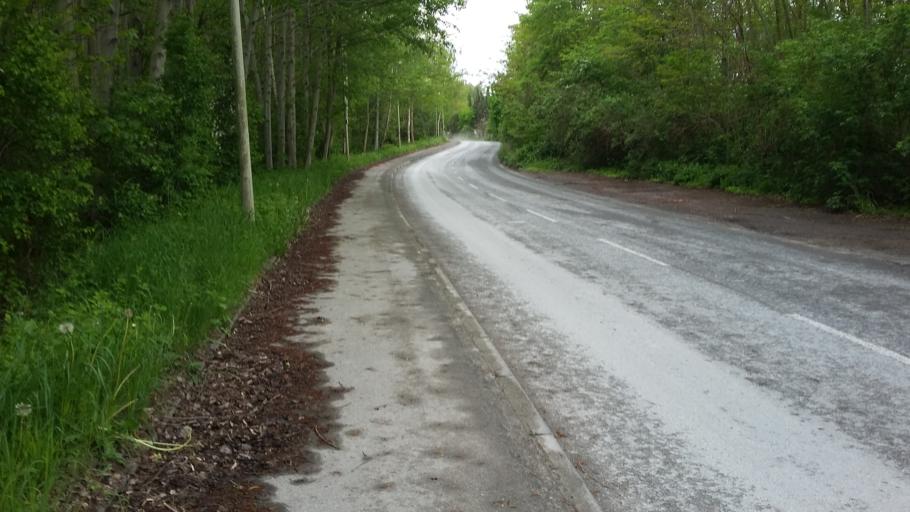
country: DE
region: North Rhine-Westphalia
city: Wulfrath
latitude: 51.2504
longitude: 7.0597
